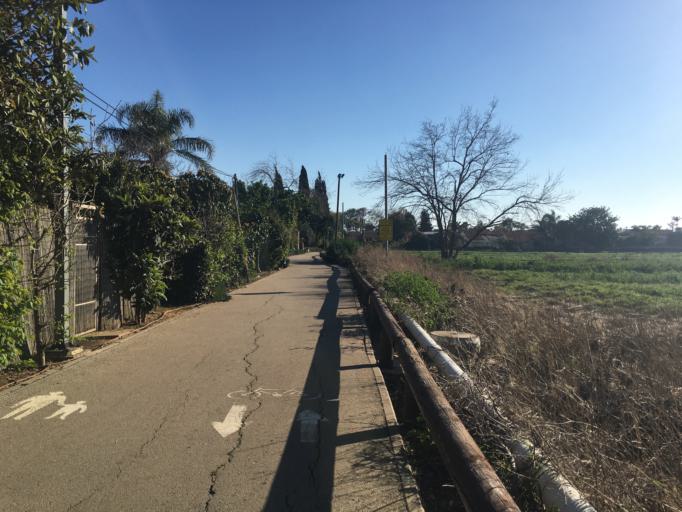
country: IL
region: Tel Aviv
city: Ramat HaSharon
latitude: 32.1434
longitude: 34.8262
